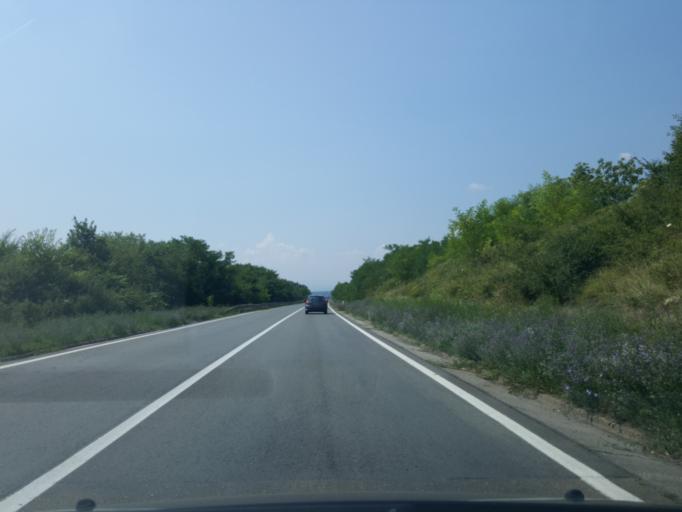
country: RS
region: Central Serbia
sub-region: Belgrade
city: Sopot
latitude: 44.5248
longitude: 20.6550
